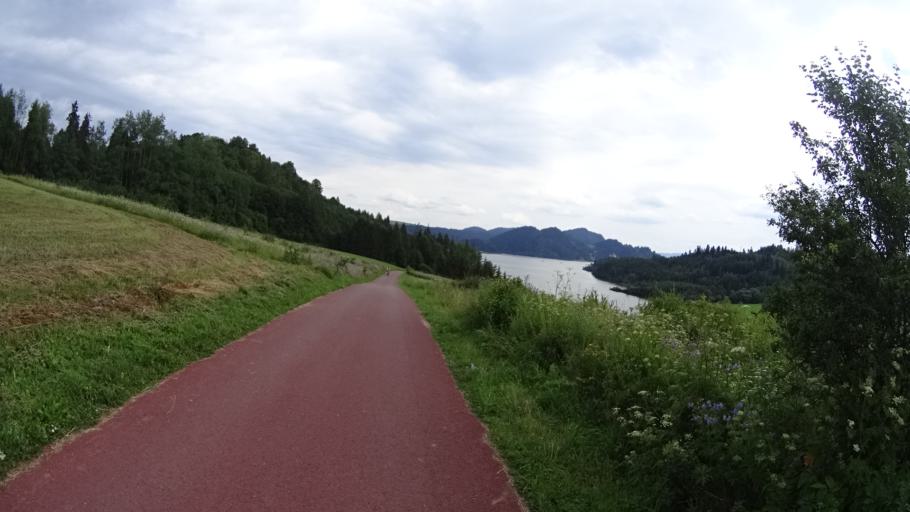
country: PL
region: Lesser Poland Voivodeship
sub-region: Powiat nowotarski
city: Niedzica
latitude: 49.4301
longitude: 20.2925
